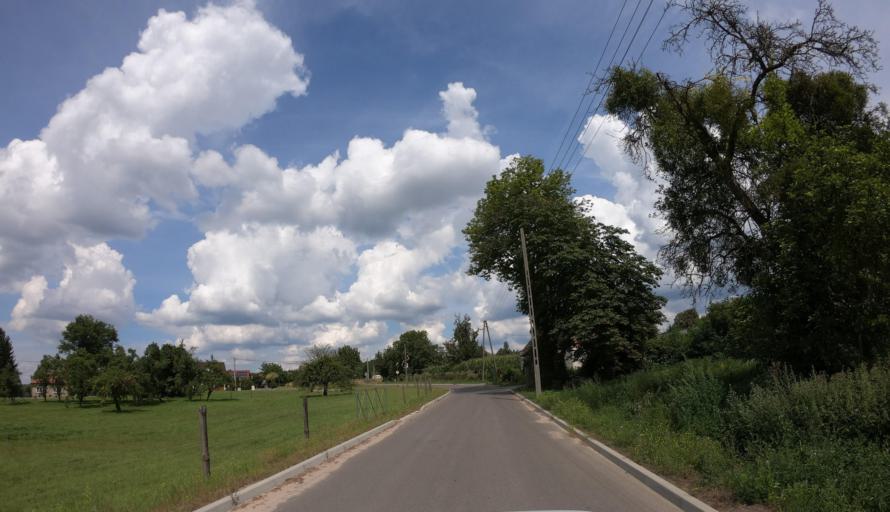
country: PL
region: West Pomeranian Voivodeship
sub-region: Powiat stargardzki
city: Kobylanka
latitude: 53.3225
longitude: 14.8249
